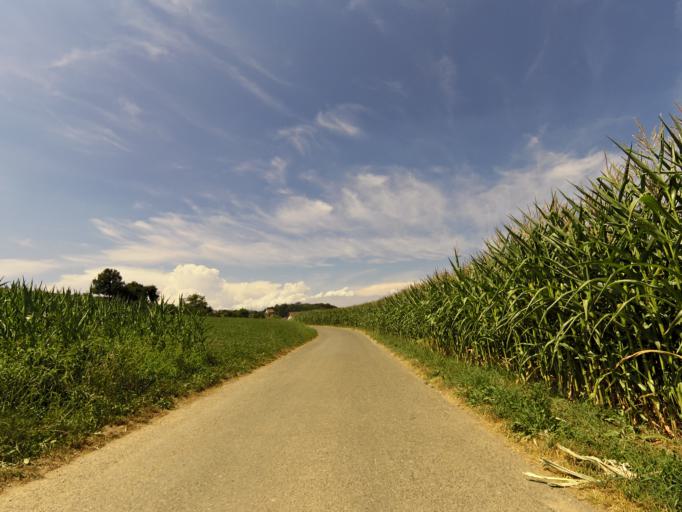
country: CH
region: Aargau
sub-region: Bezirk Bremgarten
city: Bremgarten
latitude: 47.3311
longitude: 8.3503
